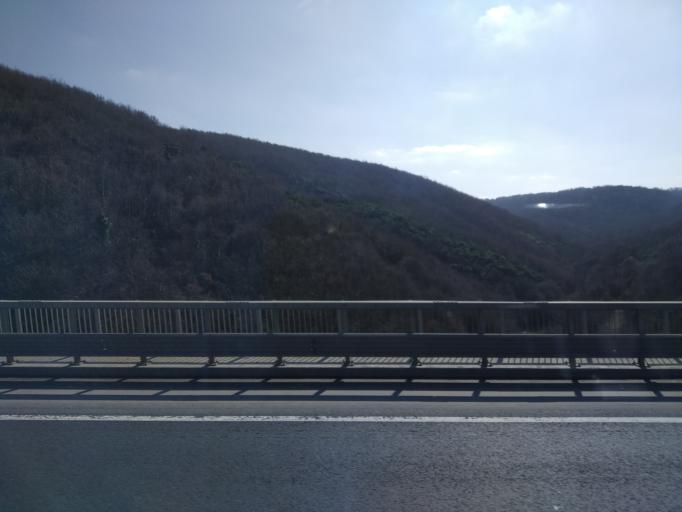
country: TR
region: Istanbul
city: Arikoey
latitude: 41.2319
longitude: 28.9490
